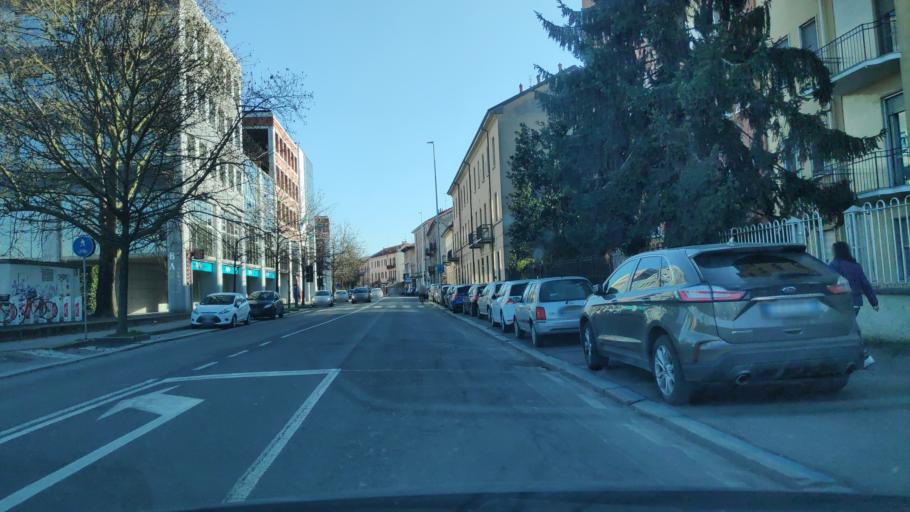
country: IT
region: Lombardy
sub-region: Provincia di Pavia
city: Pavia
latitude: 45.1949
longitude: 9.1534
